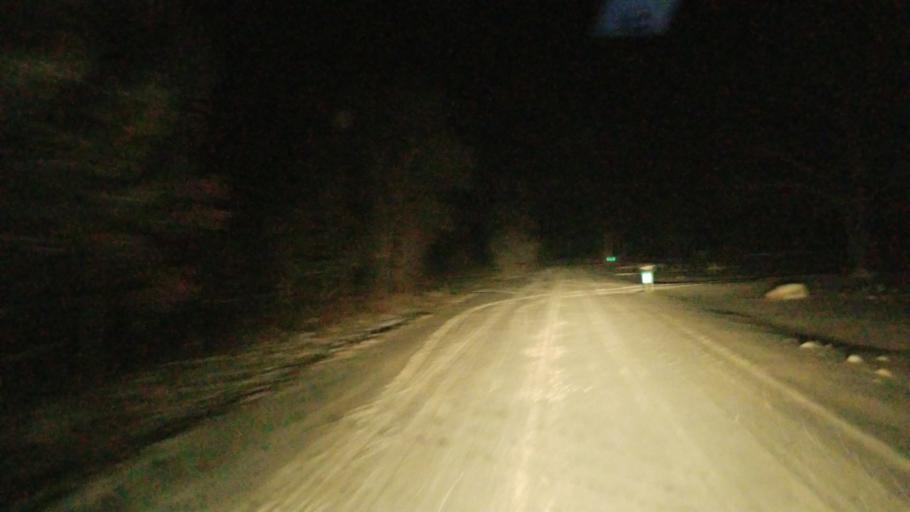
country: US
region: Michigan
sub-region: Osceola County
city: Reed City
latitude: 43.8299
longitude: -85.4141
